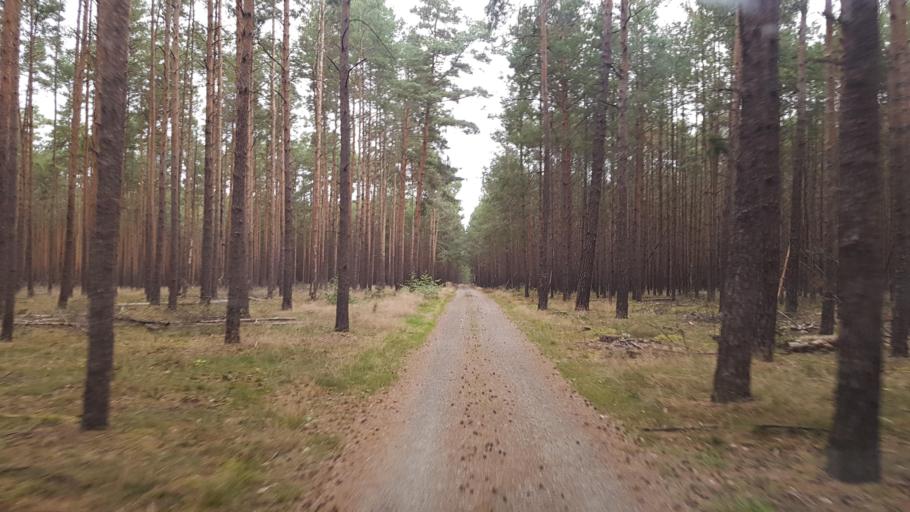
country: DE
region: Brandenburg
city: Sonnewalde
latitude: 51.7368
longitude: 13.6575
